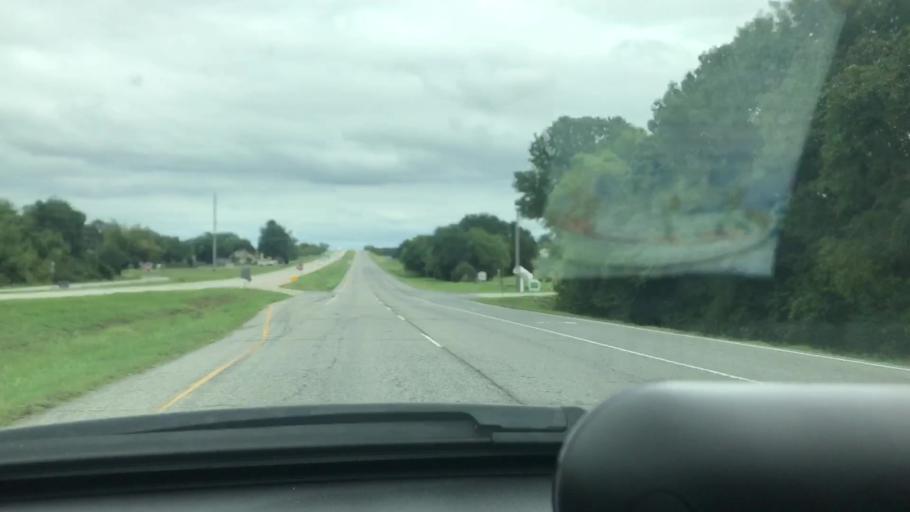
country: US
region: Oklahoma
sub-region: Wagoner County
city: Wagoner
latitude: 35.9711
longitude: -95.3872
